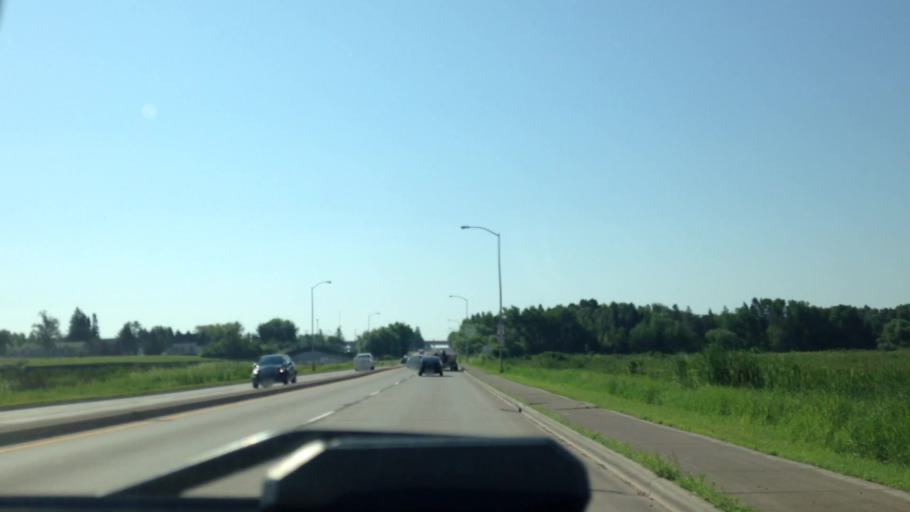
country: US
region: Wisconsin
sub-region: Douglas County
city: Superior
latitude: 46.6953
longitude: -92.0331
